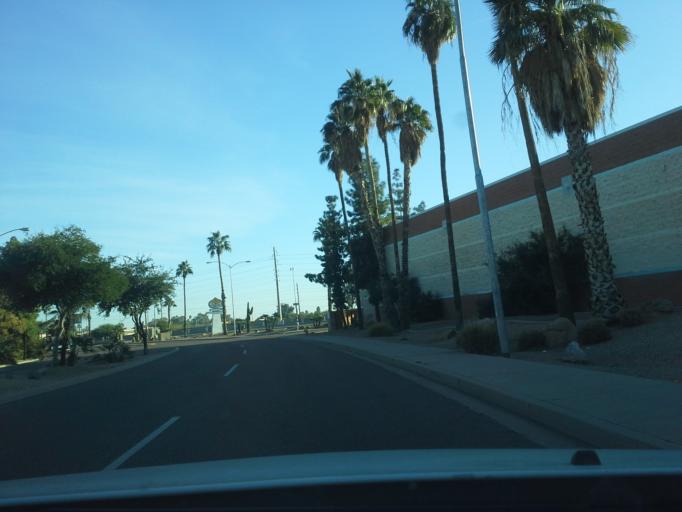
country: US
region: Arizona
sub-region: Maricopa County
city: Glendale
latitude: 33.5727
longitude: -112.1242
